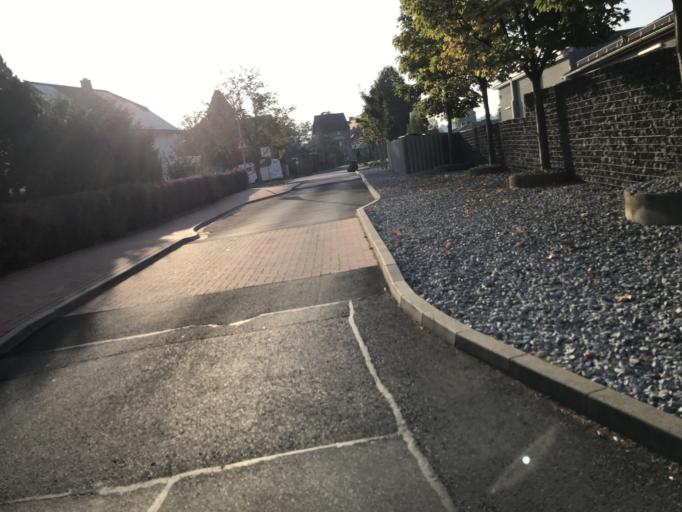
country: DE
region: Hesse
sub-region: Regierungsbezirk Kassel
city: Guxhagen
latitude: 51.2030
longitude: 9.4733
